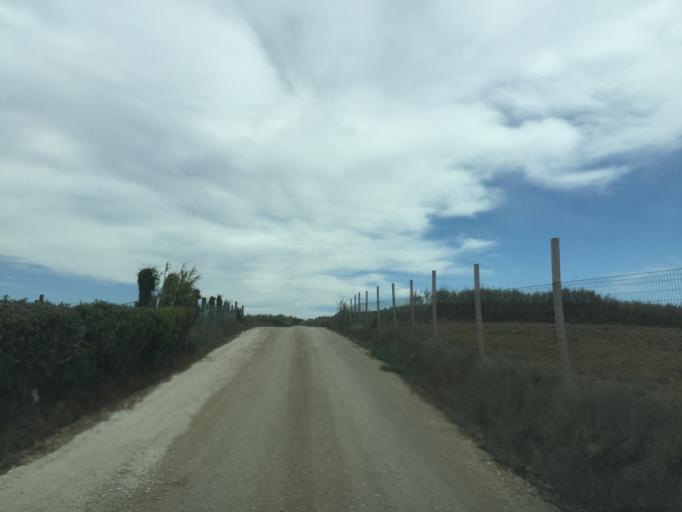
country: PT
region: Lisbon
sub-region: Lourinha
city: Lourinha
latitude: 39.1964
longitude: -9.3433
